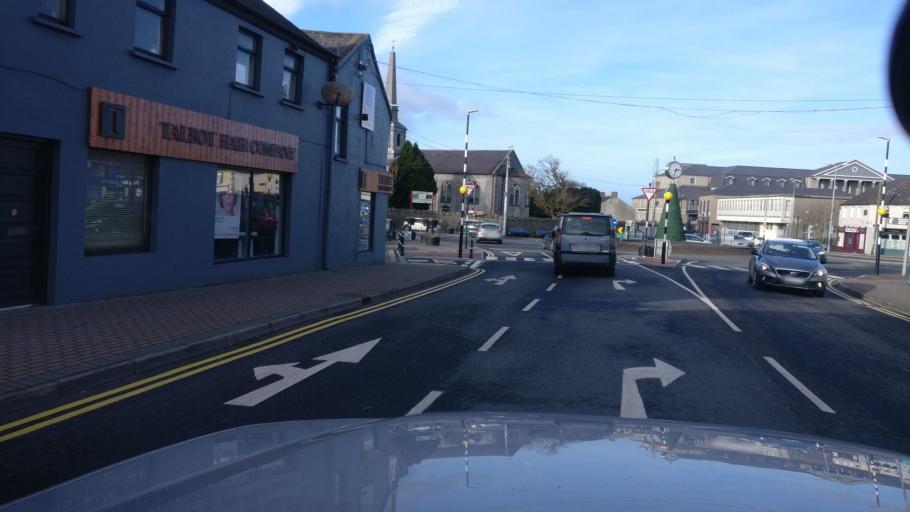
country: IE
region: Leinster
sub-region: Laois
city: Portlaoise
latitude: 53.0332
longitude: -7.3026
